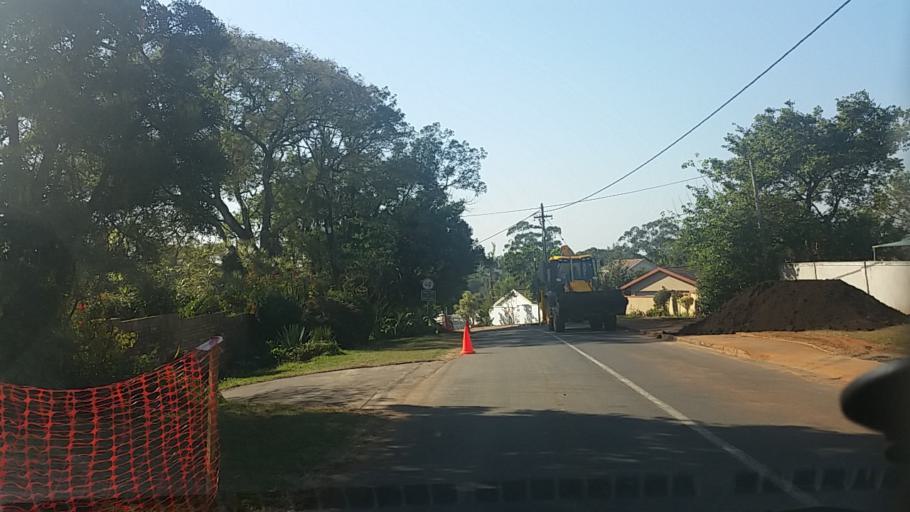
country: ZA
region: KwaZulu-Natal
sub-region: eThekwini Metropolitan Municipality
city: Berea
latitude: -29.8422
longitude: 30.9138
